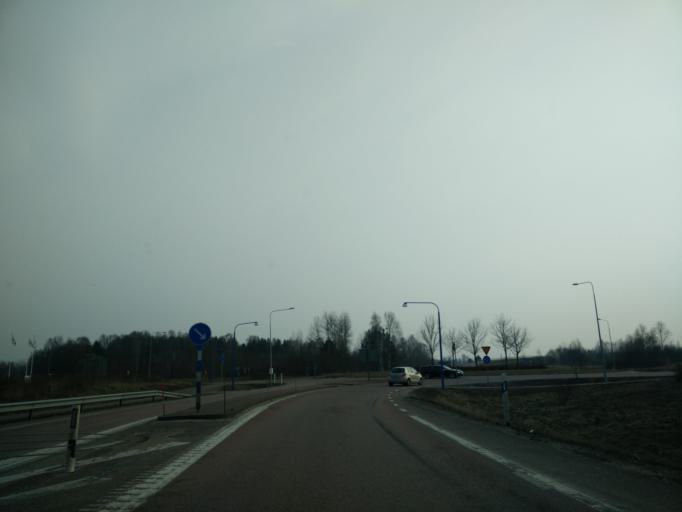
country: SE
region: Vaermland
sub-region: Karlstads Kommun
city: Karlstad
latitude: 59.4301
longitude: 13.4114
